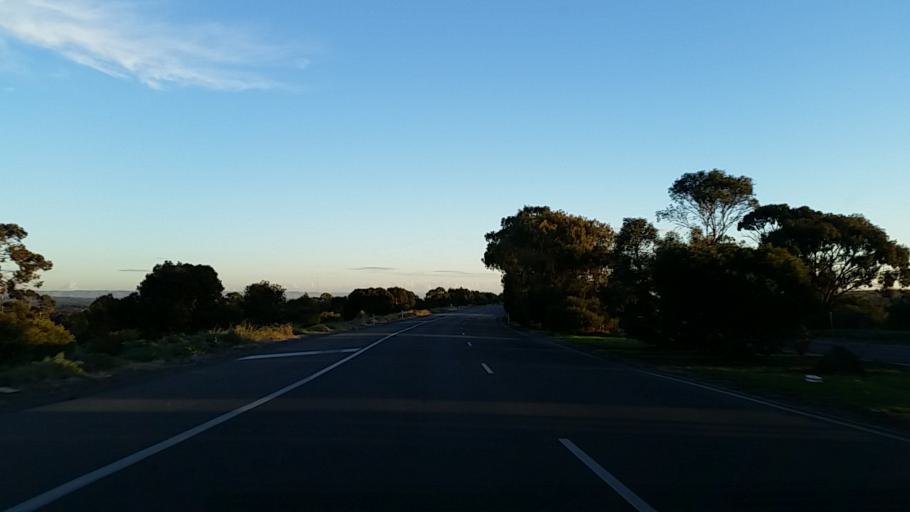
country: AU
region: South Australia
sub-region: Marion
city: Trott Park
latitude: -35.0631
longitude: 138.5346
